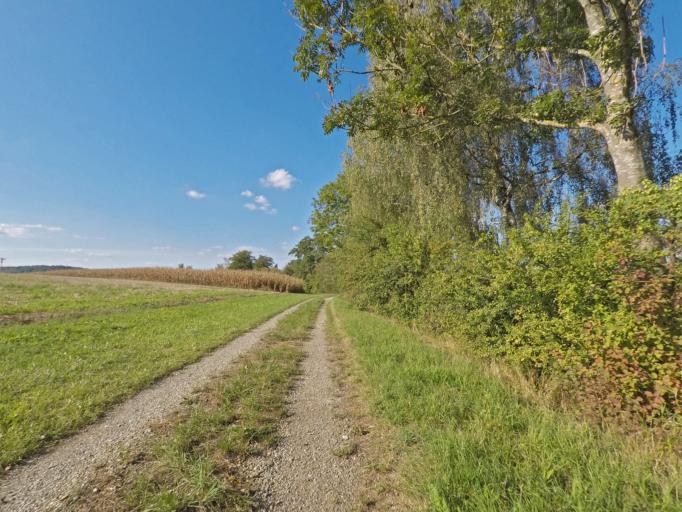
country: CH
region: Thurgau
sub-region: Frauenfeld District
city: Diessenhofen
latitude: 47.6623
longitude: 8.7472
